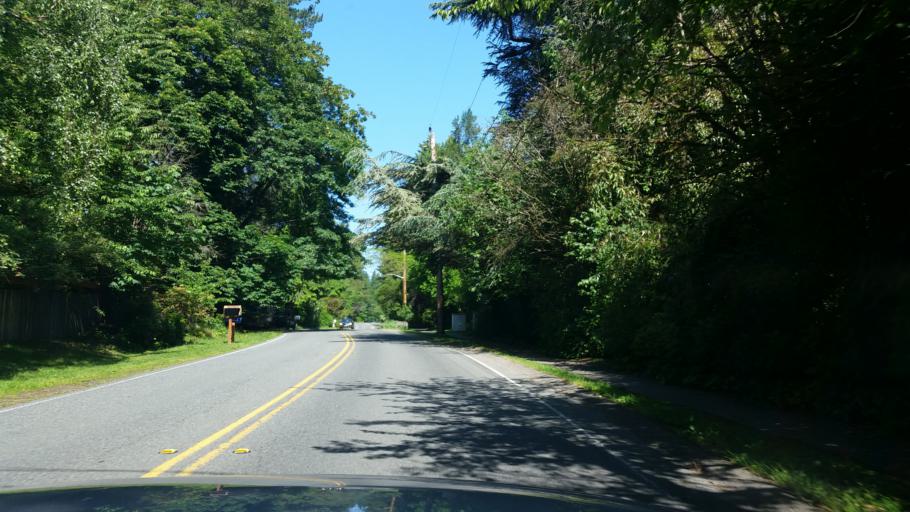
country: US
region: Washington
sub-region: King County
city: Lake Forest Park
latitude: 47.7529
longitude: -122.2824
